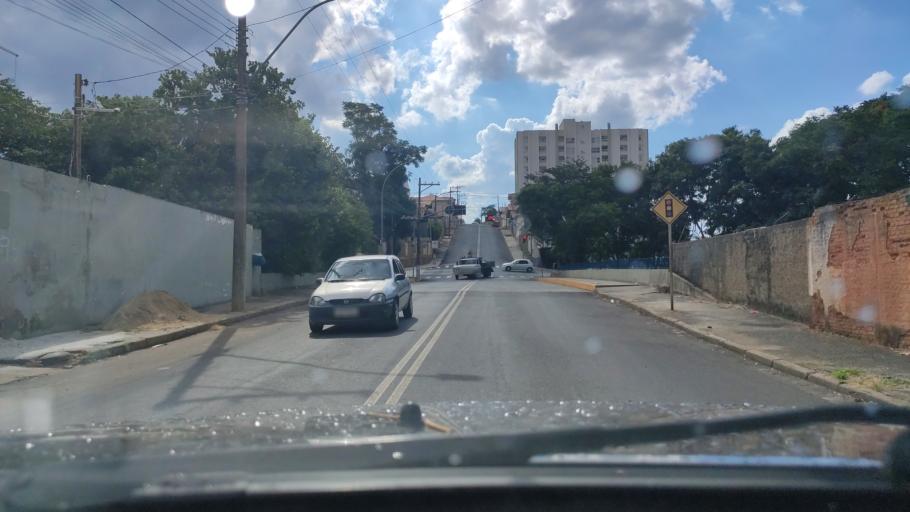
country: BR
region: Sao Paulo
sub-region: Itapira
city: Itapira
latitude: -22.4377
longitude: -46.8179
